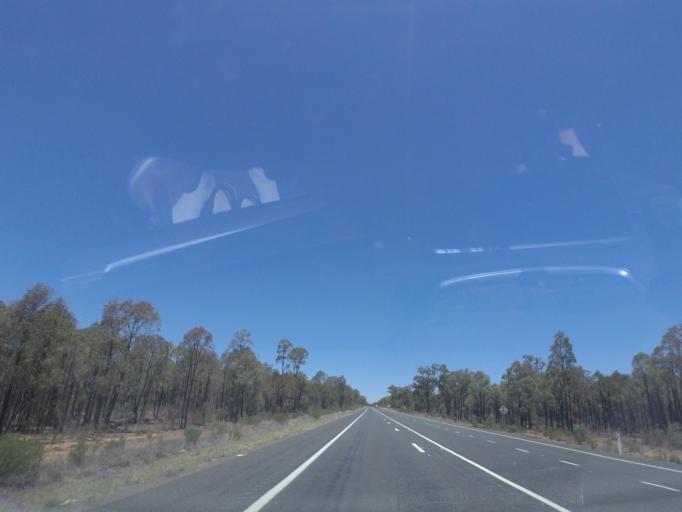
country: AU
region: New South Wales
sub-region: Warrumbungle Shire
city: Coonabarabran
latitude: -30.8681
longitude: 149.4513
